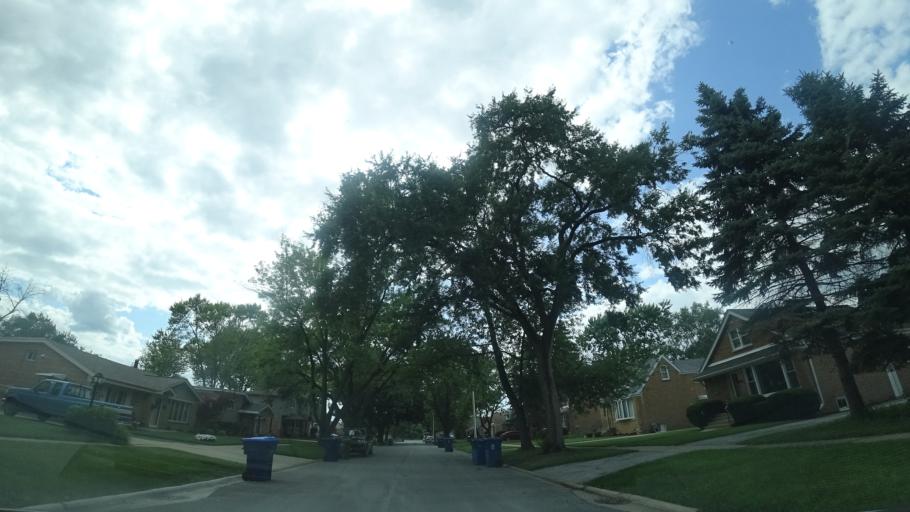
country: US
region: Illinois
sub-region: Cook County
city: Alsip
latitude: 41.6929
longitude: -87.7281
